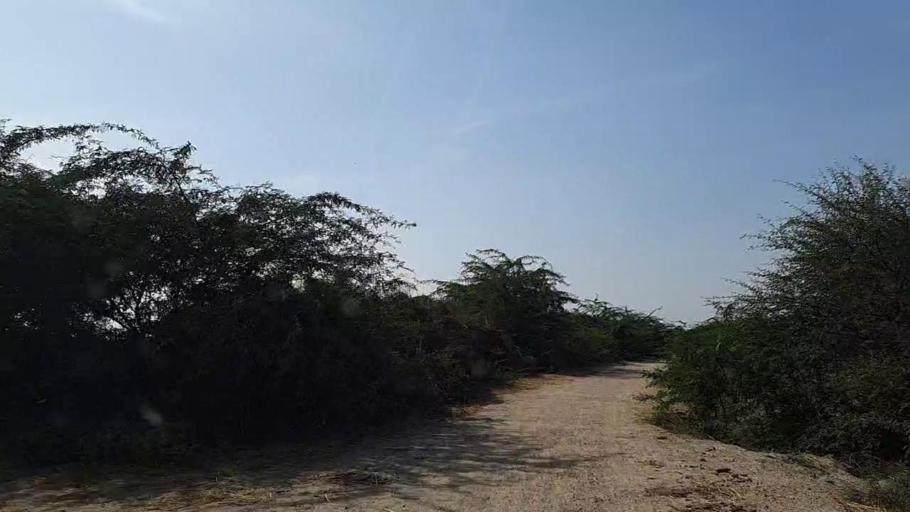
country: PK
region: Sindh
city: Daro Mehar
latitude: 24.7032
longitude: 68.1567
